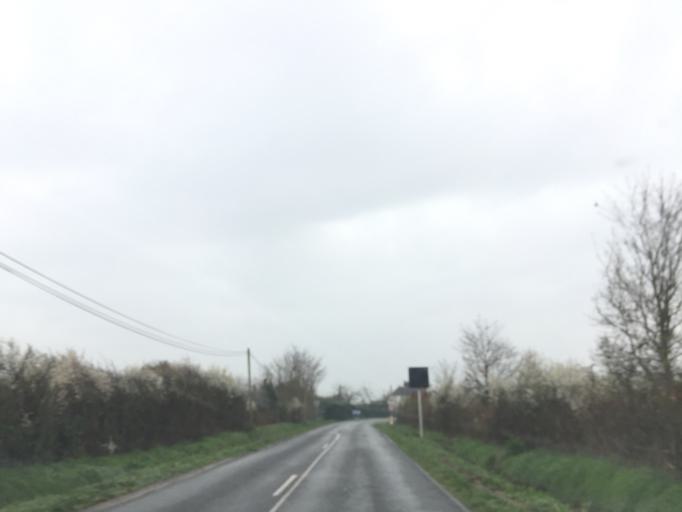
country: FR
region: Pays de la Loire
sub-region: Departement de la Loire-Atlantique
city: Casson
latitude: 47.3977
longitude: -1.5274
